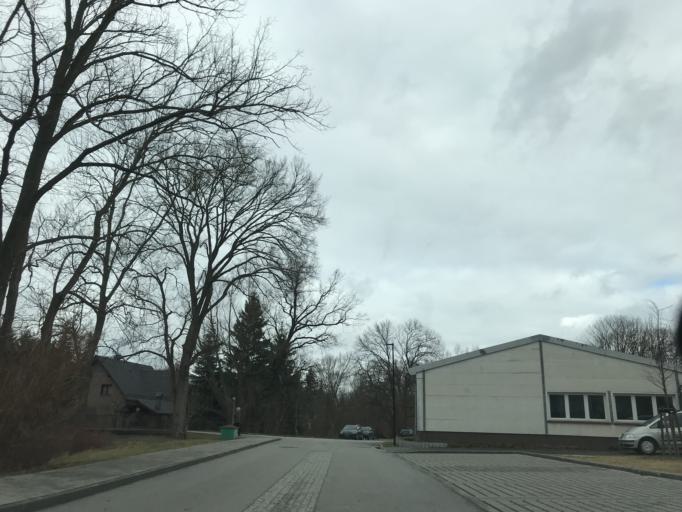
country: DE
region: Brandenburg
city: Luebben
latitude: 51.9425
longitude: 13.9011
